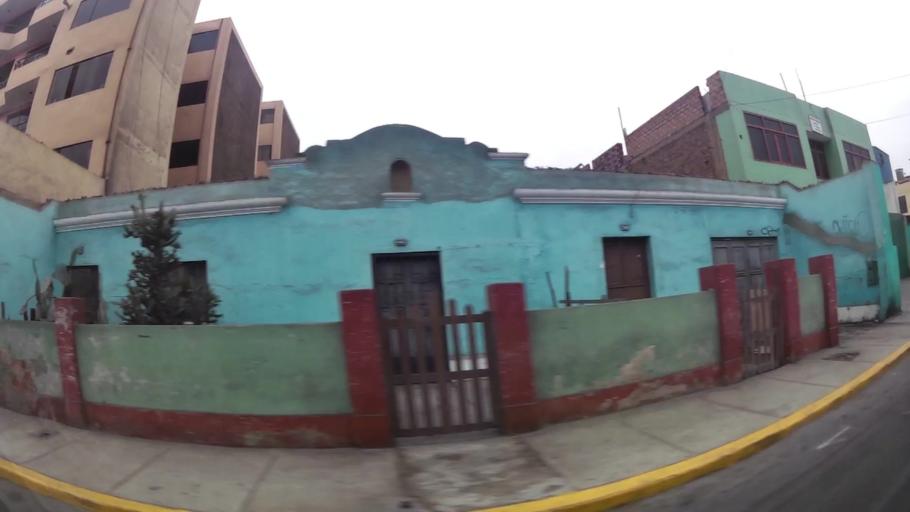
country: PE
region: Callao
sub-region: Callao
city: Callao
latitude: -12.0878
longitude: -77.0882
